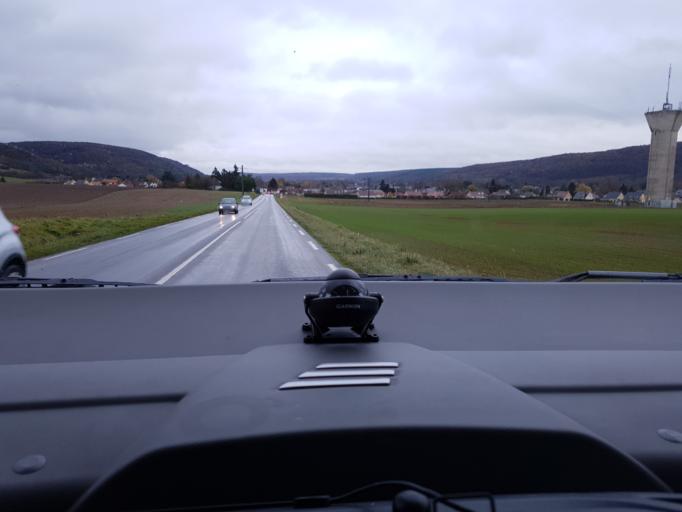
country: FR
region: Haute-Normandie
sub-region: Departement de l'Eure
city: Romilly-sur-Andelle
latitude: 49.3300
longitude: 1.2412
